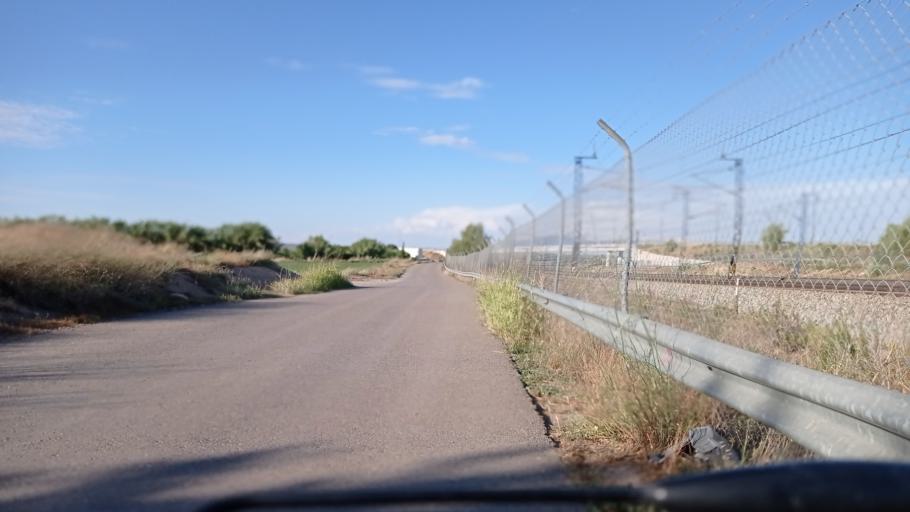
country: ES
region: Aragon
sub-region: Provincia de Zaragoza
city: Oliver-Valdefierro, Oliver, Valdefierro
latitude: 41.6555
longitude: -0.9573
